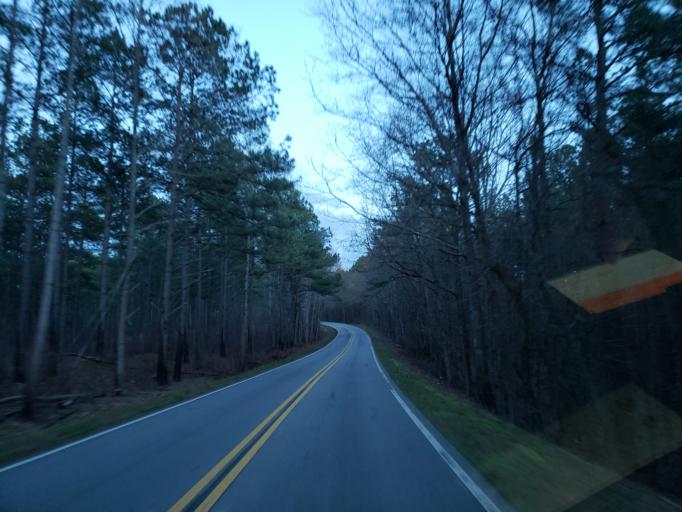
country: US
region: Georgia
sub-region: Polk County
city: Rockmart
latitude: 33.9896
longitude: -84.9430
